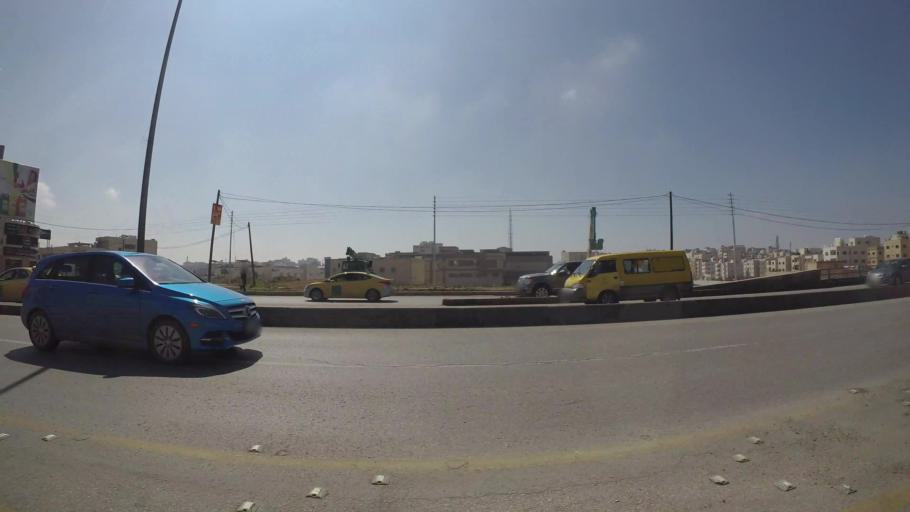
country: JO
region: Amman
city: Al Bunayyat ash Shamaliyah
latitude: 31.9185
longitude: 35.8982
